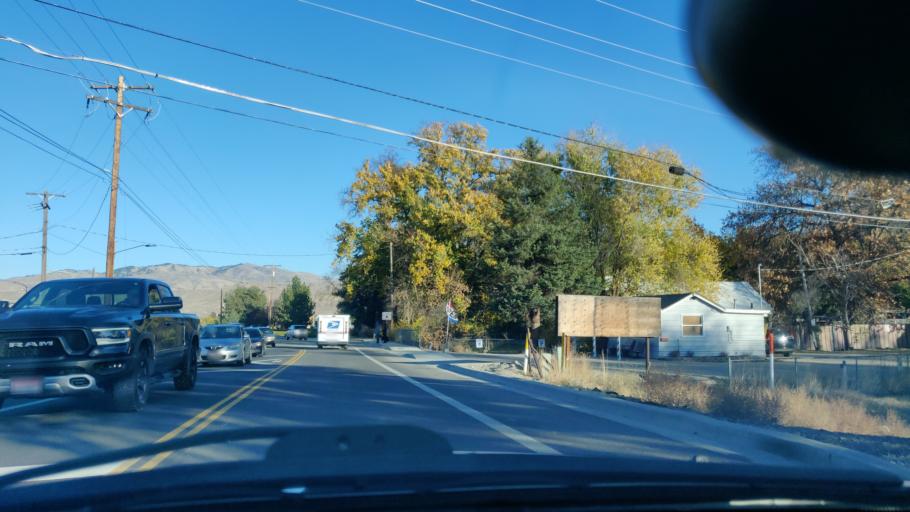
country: US
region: Idaho
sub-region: Ada County
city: Boise
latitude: 43.5935
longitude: -116.2083
